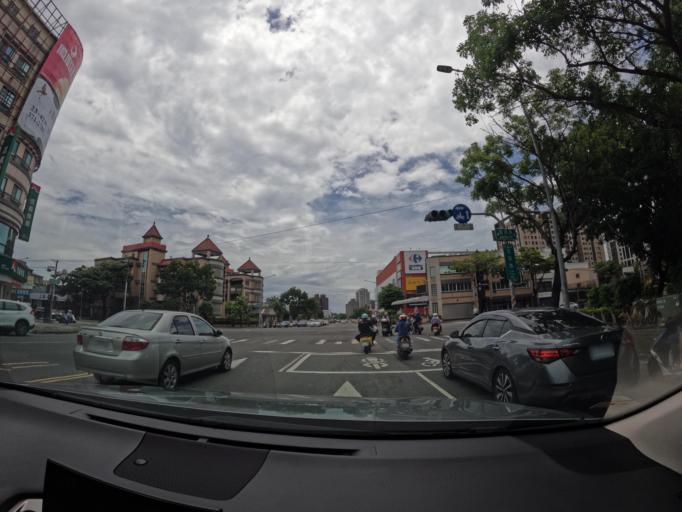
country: TW
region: Kaohsiung
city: Kaohsiung
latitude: 22.7272
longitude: 120.2920
